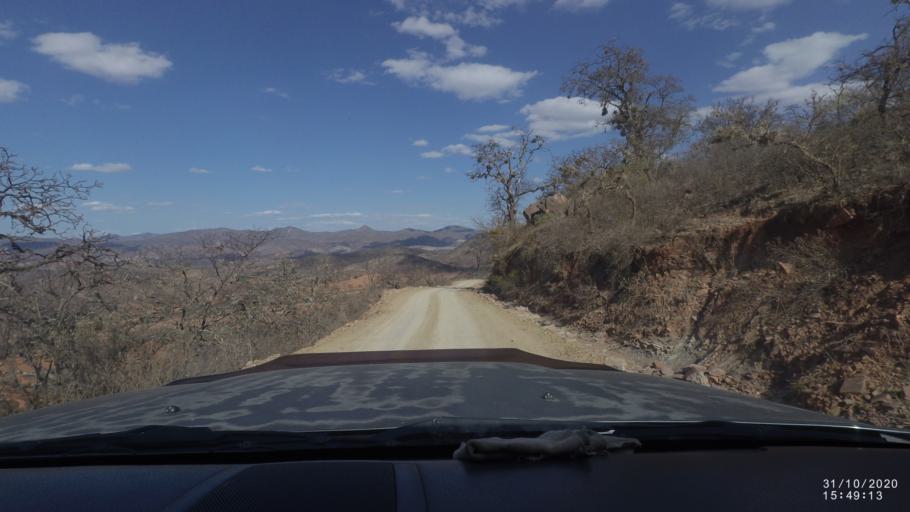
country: BO
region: Chuquisaca
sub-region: Provincia Zudanez
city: Mojocoya
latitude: -18.3101
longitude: -64.7088
